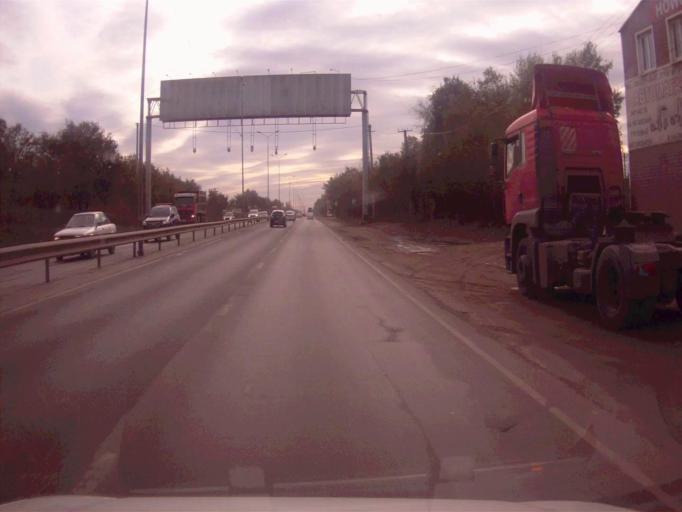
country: RU
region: Chelyabinsk
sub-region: Gorod Chelyabinsk
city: Chelyabinsk
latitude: 55.1088
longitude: 61.4087
